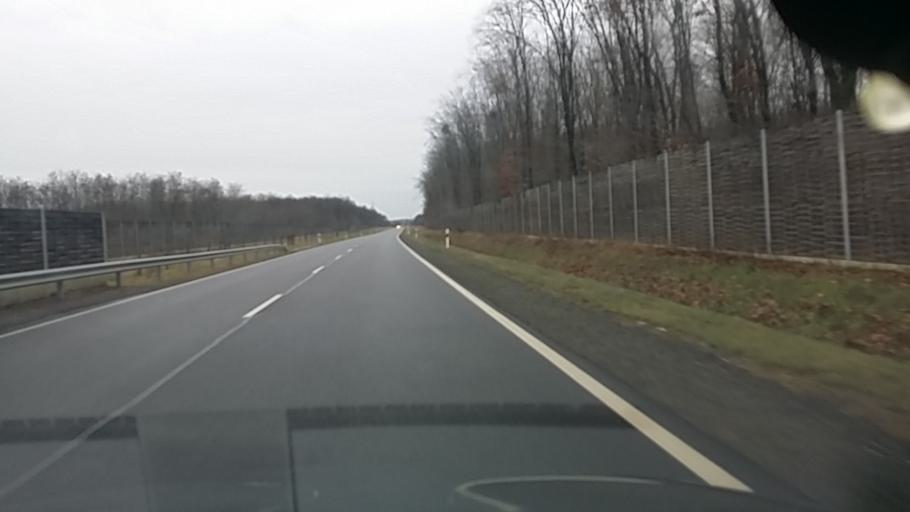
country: HU
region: Hajdu-Bihar
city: Hajduhadhaz
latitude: 47.6160
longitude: 21.6356
